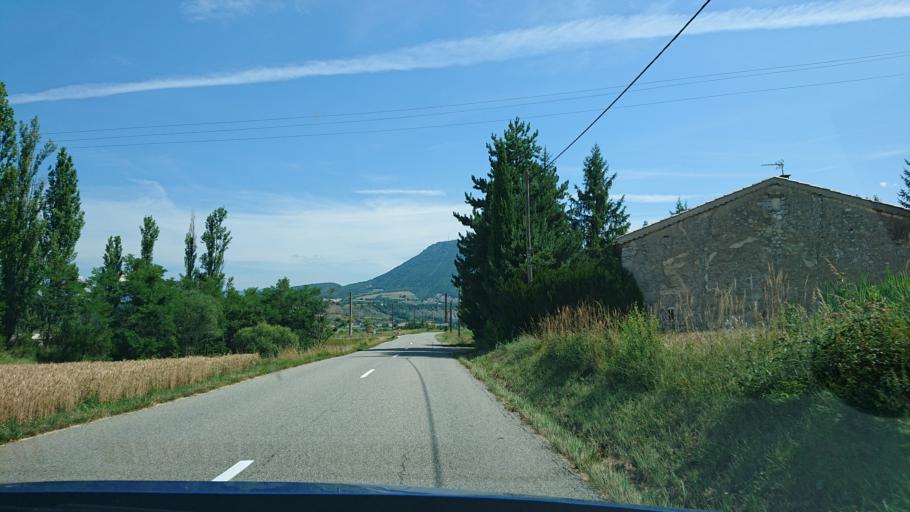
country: FR
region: Provence-Alpes-Cote d'Azur
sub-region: Departement des Alpes-de-Haute-Provence
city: Sisteron
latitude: 44.2464
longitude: 5.9511
